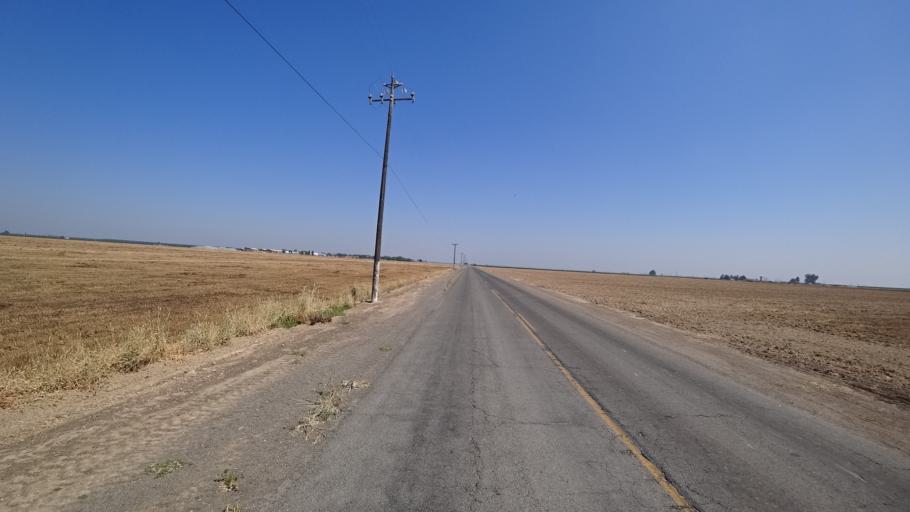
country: US
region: California
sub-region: Tulare County
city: London
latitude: 36.4024
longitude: -119.5288
